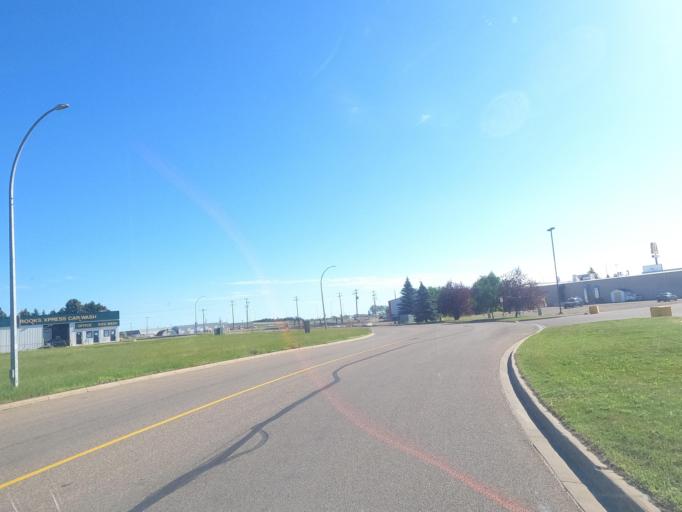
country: CA
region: Alberta
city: Brooks
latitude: 50.5855
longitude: -111.8997
